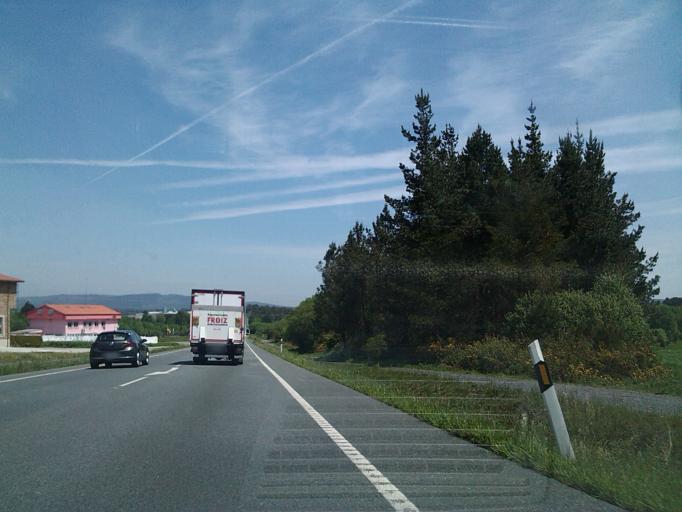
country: ES
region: Galicia
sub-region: Provincia da Coruna
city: Curtis
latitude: 43.1426
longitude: -8.0236
